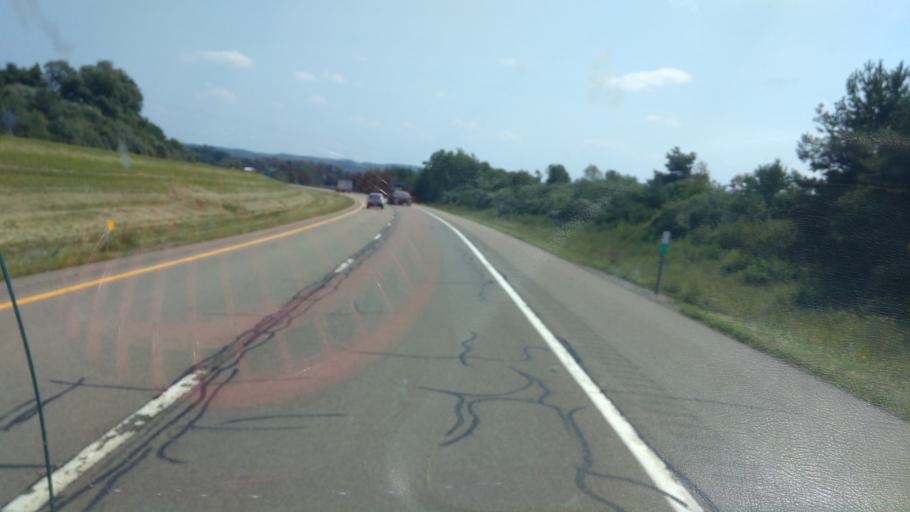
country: US
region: New York
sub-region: Steuben County
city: Canisteo
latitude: 42.3695
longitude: -77.5208
